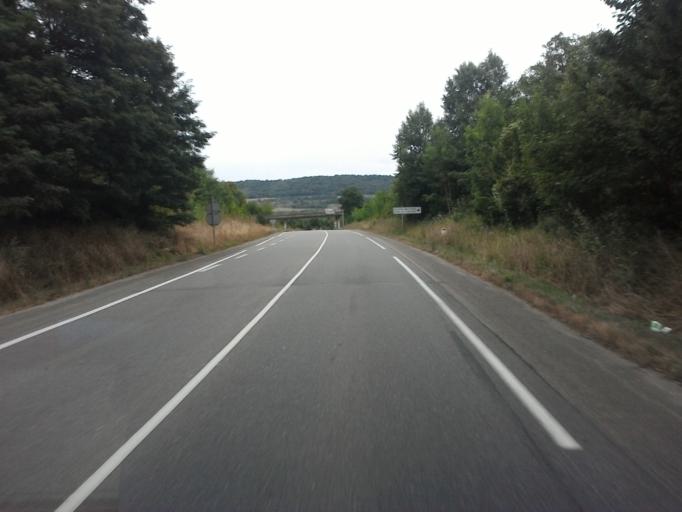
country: FR
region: Lorraine
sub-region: Departement de Meurthe-et-Moselle
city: Pont-Saint-Vincent
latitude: 48.5976
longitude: 6.1138
